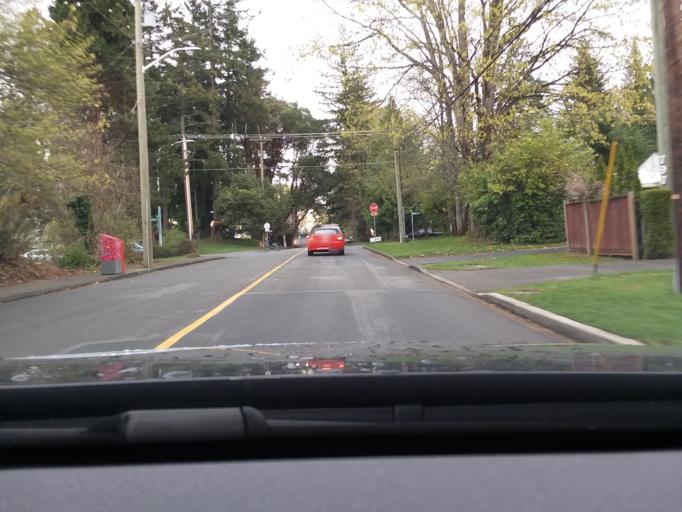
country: CA
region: British Columbia
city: Victoria
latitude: 48.5142
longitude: -123.3749
